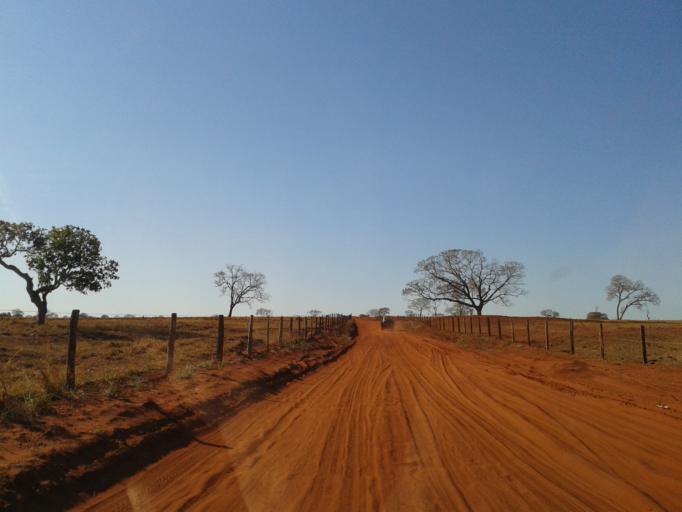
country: BR
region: Minas Gerais
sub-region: Ituiutaba
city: Ituiutaba
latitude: -18.9773
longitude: -49.4105
